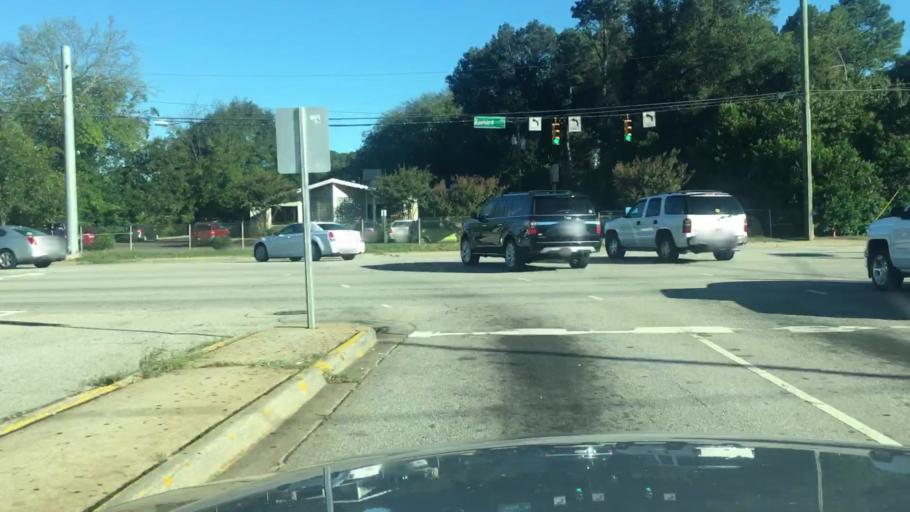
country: US
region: North Carolina
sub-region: Cumberland County
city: Fayetteville
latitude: 35.0438
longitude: -78.9401
